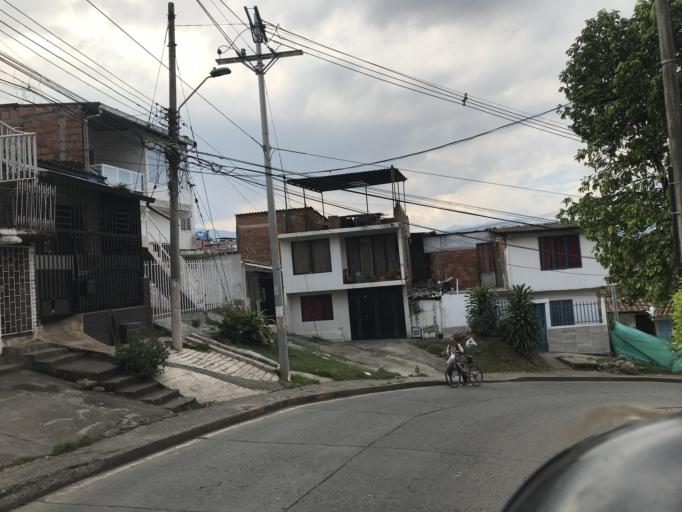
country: CO
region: Valle del Cauca
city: Cali
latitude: 3.3747
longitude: -76.5527
